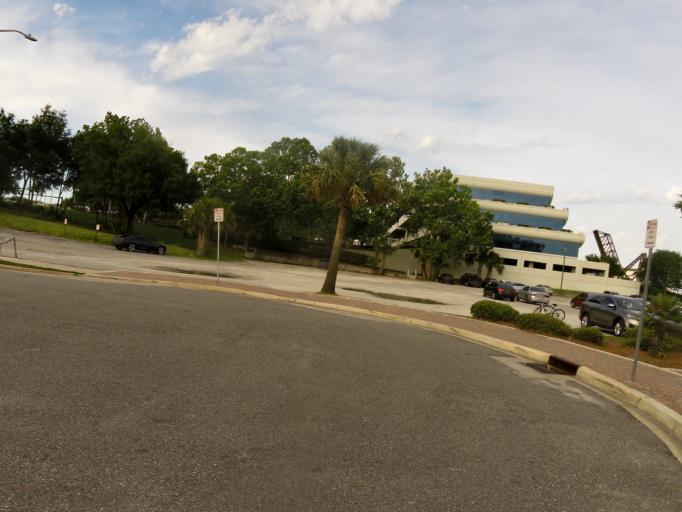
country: US
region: Florida
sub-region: Duval County
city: Jacksonville
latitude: 30.3217
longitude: -81.6713
